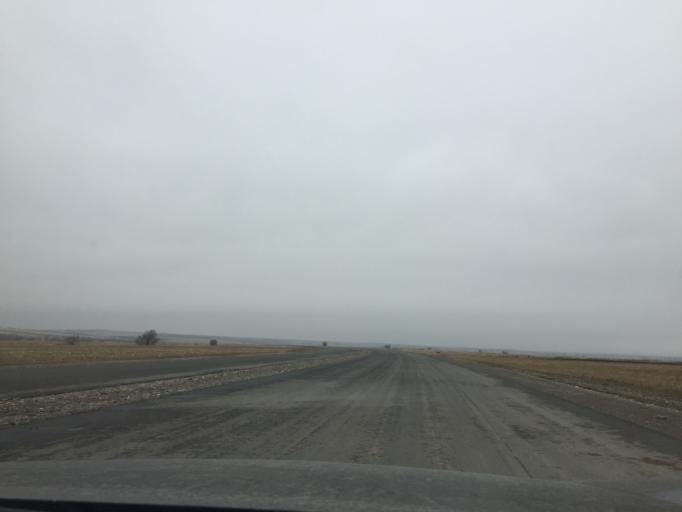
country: KZ
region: Ongtustik Qazaqstan
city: Turar Ryskulov
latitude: 42.5182
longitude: 70.3257
